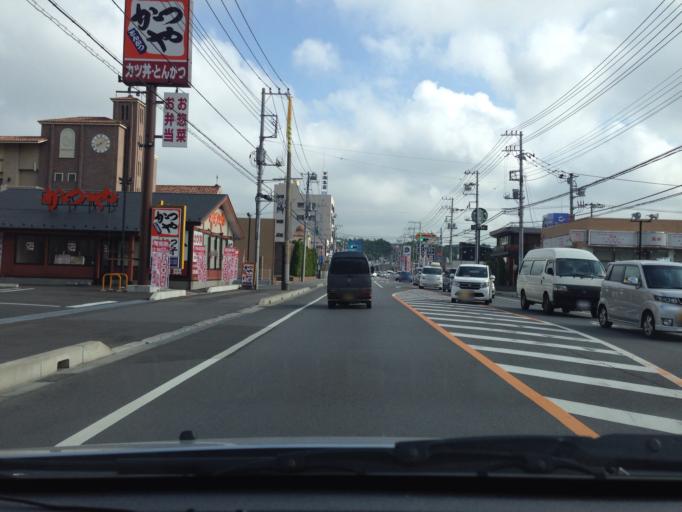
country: JP
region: Ibaraki
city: Naka
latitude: 36.0906
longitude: 140.2078
